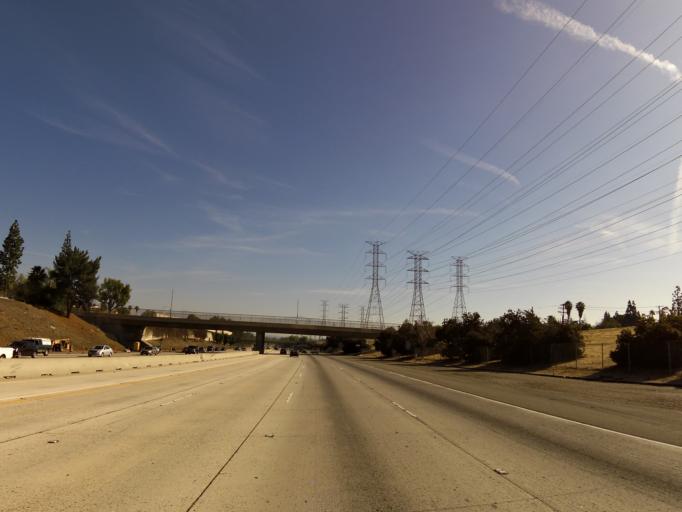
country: US
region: California
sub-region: Los Angeles County
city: Northridge
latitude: 34.2776
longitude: -118.5171
